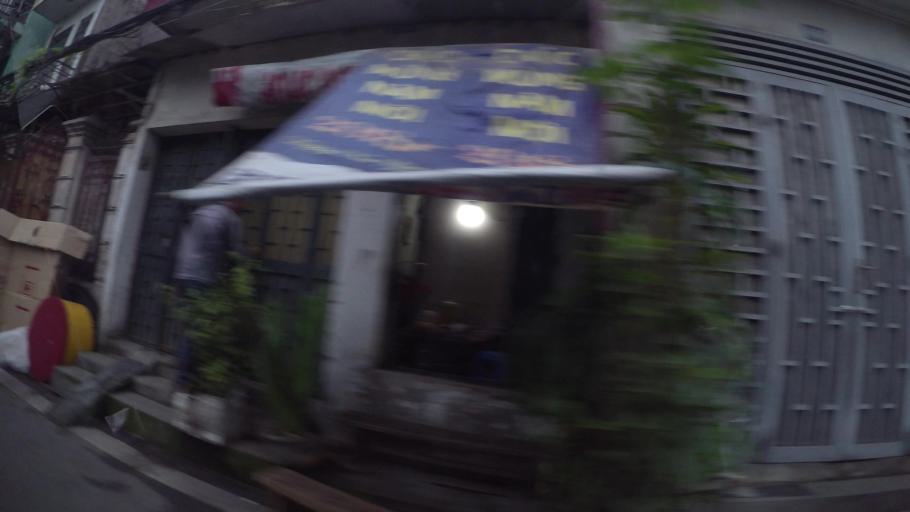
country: VN
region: Ha Noi
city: Hai BaTrung
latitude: 21.0152
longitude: 105.8653
